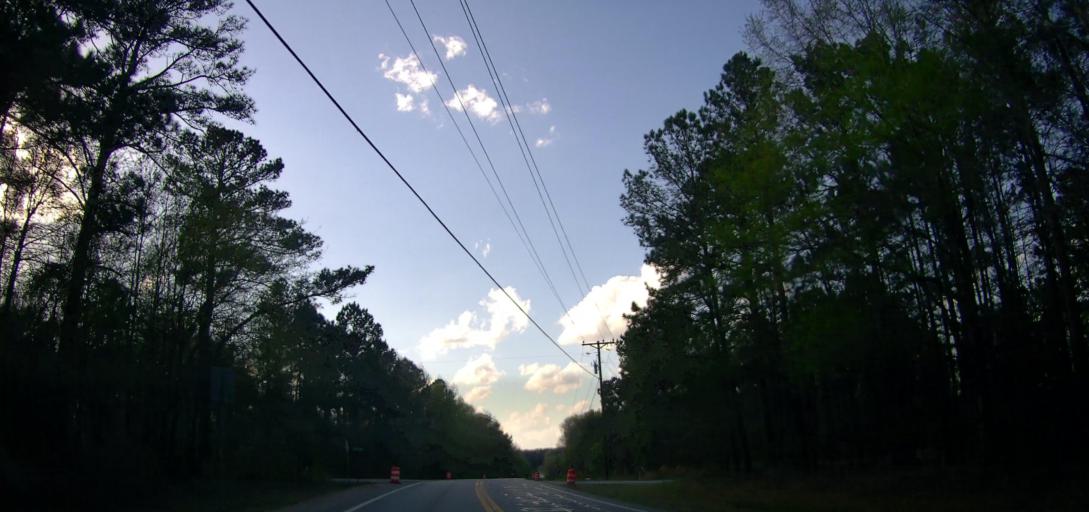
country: US
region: Georgia
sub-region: Putnam County
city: Eatonton
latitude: 33.1768
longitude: -83.4042
